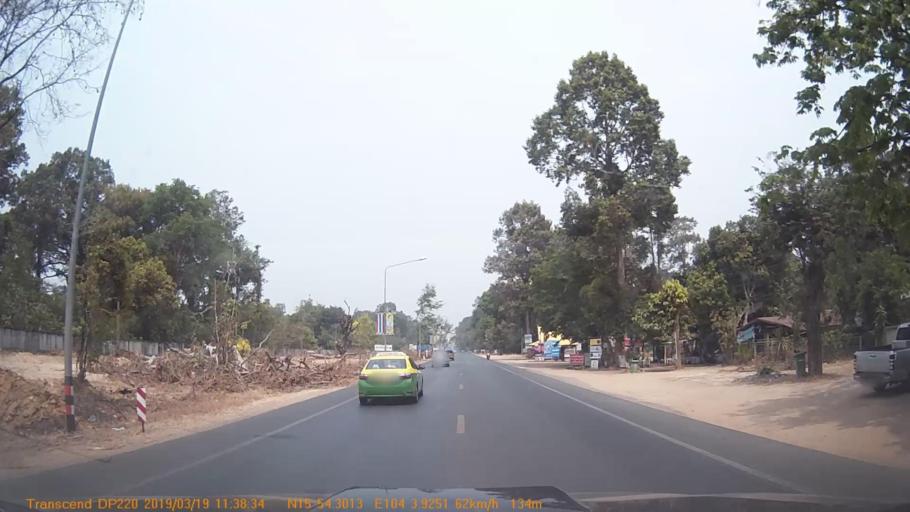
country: TH
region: Yasothon
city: Yasothon
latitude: 15.9052
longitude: 104.0653
